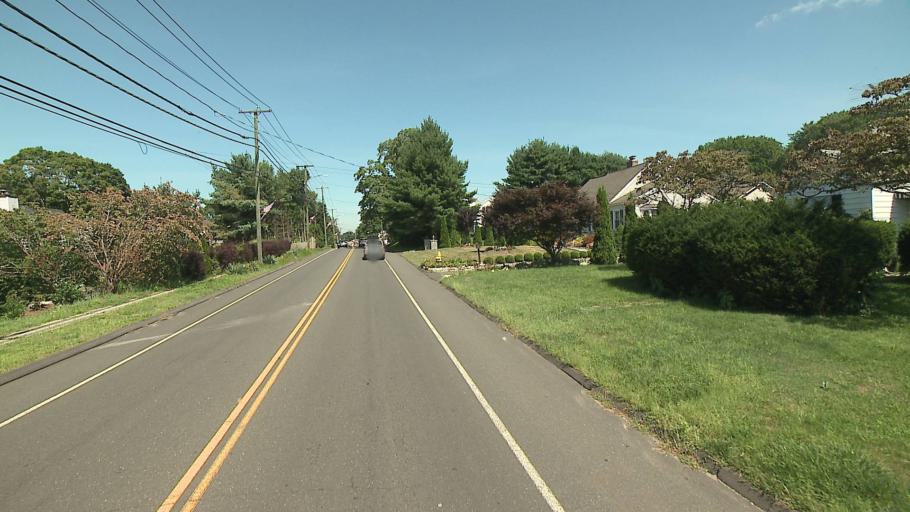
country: US
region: Connecticut
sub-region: Fairfield County
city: Trumbull
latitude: 41.2678
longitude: -73.2251
